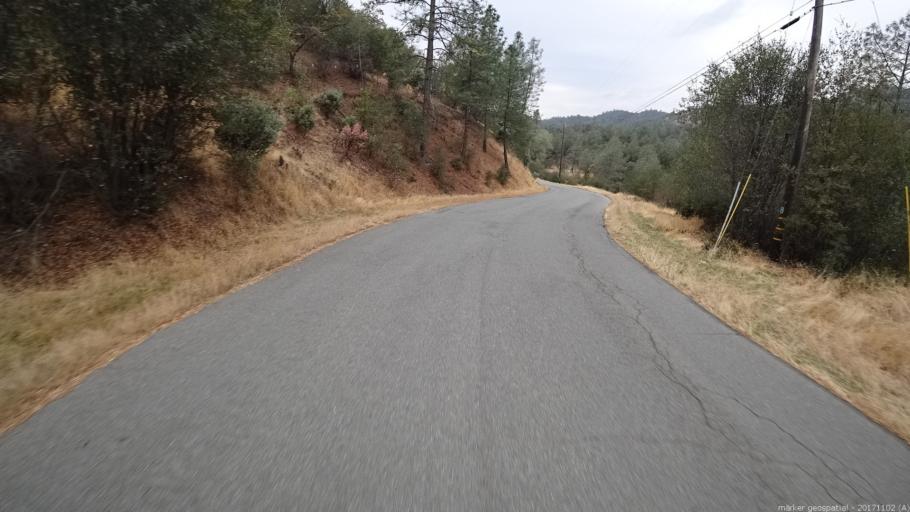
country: US
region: California
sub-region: Shasta County
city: Bella Vista
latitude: 40.7197
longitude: -122.2389
